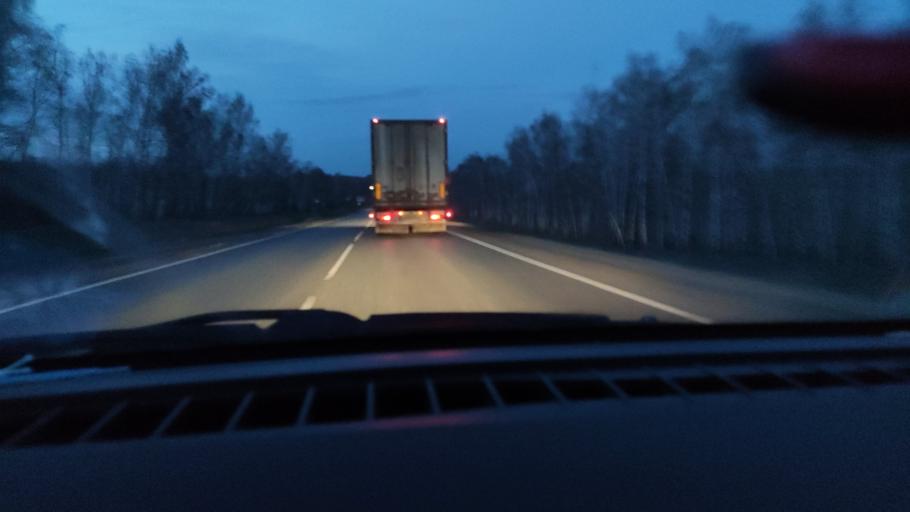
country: RU
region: Saratov
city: Sennoy
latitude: 52.1236
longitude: 46.8500
